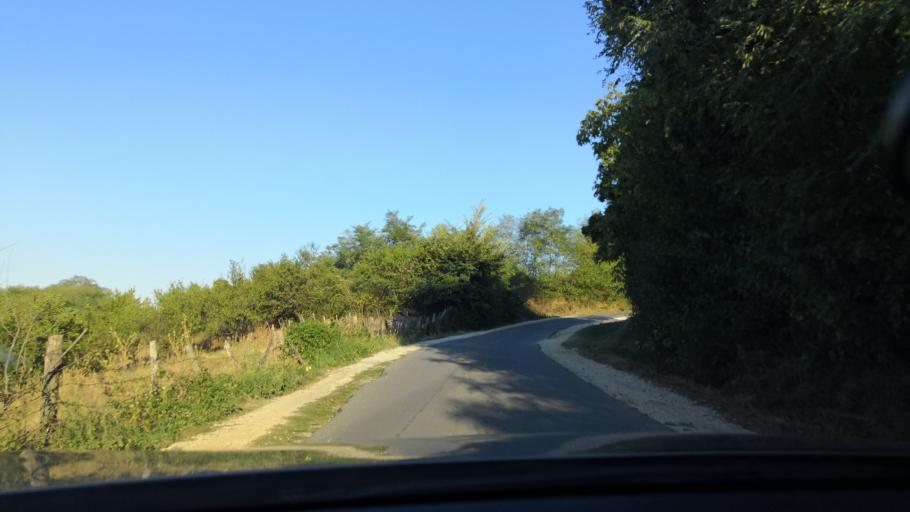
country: RS
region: Central Serbia
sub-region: Sumadijski Okrug
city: Arangelovac
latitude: 44.3311
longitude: 20.5755
